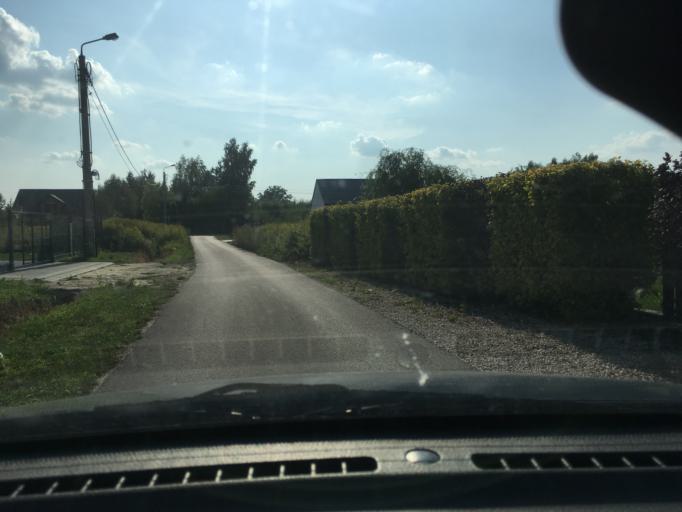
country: PL
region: Masovian Voivodeship
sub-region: Powiat piaseczynski
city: Lesznowola
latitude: 52.0519
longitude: 20.9331
